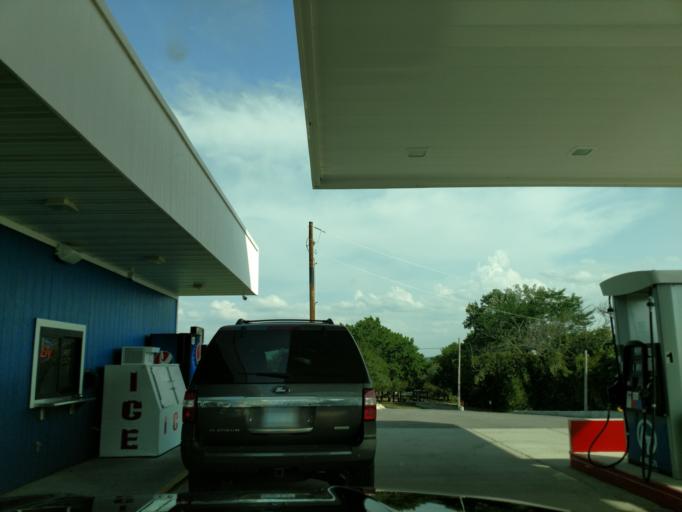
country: US
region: Missouri
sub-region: Barry County
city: Shell Knob
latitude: 36.6065
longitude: -93.5668
